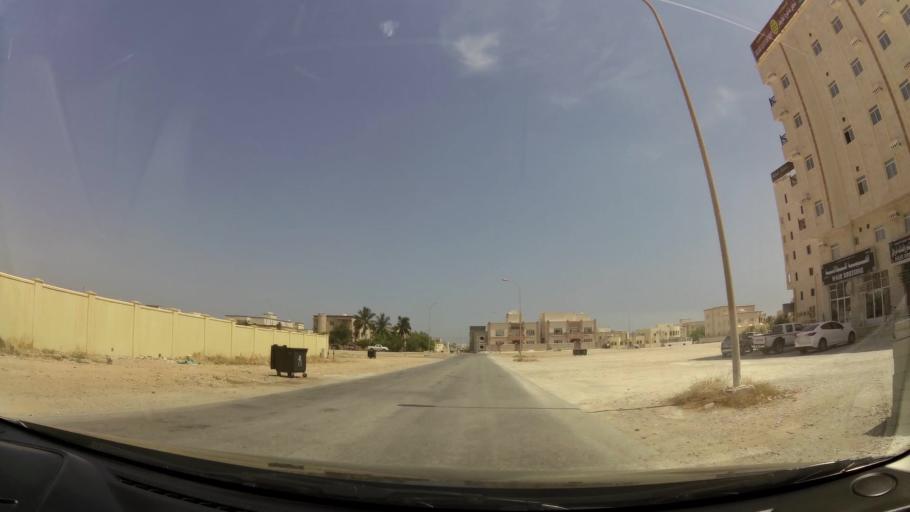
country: OM
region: Zufar
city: Salalah
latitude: 17.0511
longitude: 54.1571
